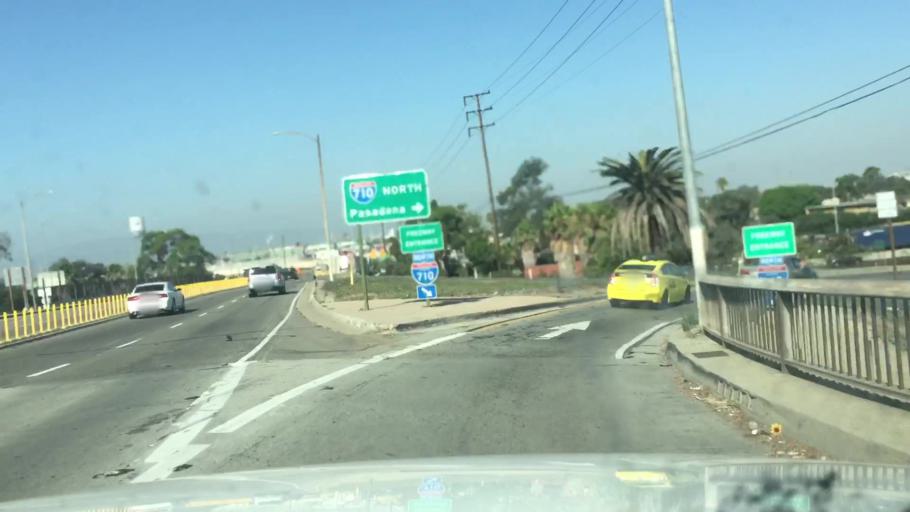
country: US
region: California
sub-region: Los Angeles County
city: Long Beach
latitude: 33.7902
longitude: -118.2064
